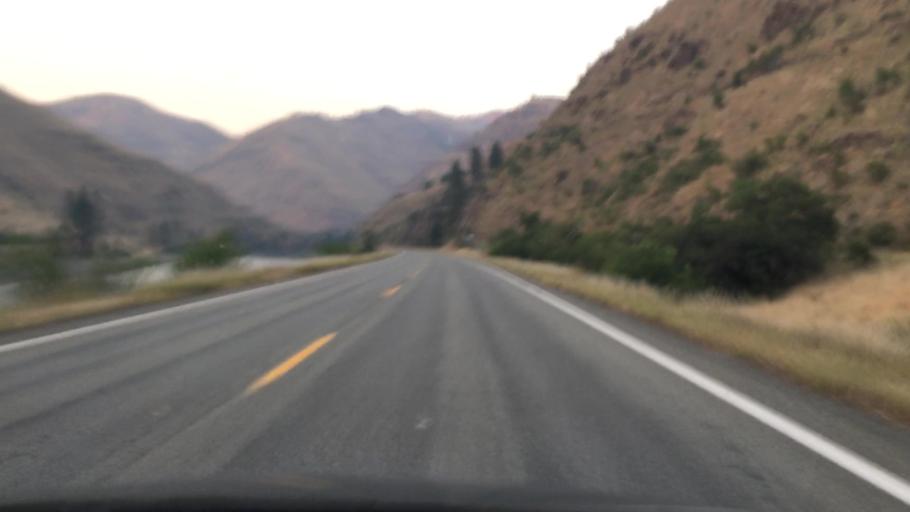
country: US
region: Idaho
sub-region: Idaho County
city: Grangeville
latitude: 45.5895
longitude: -116.2882
